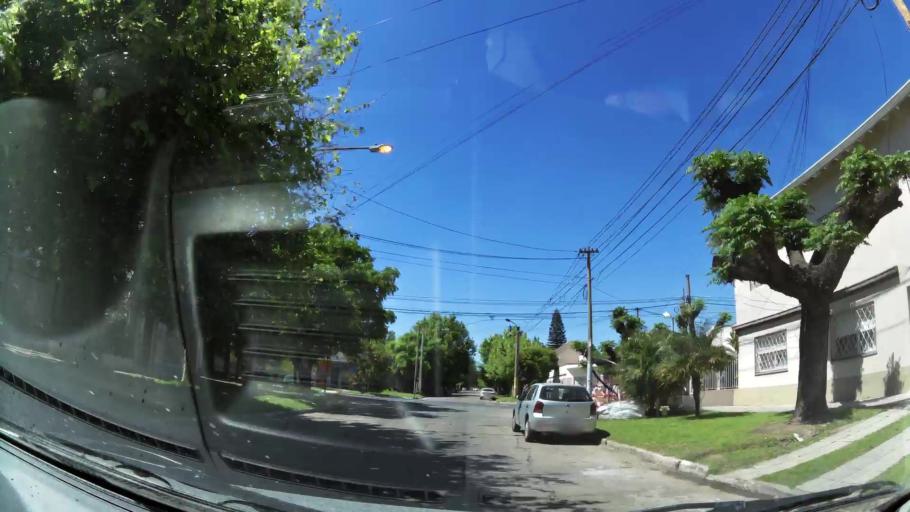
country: AR
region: Buenos Aires
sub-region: Partido de Quilmes
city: Quilmes
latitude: -34.7173
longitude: -58.2676
